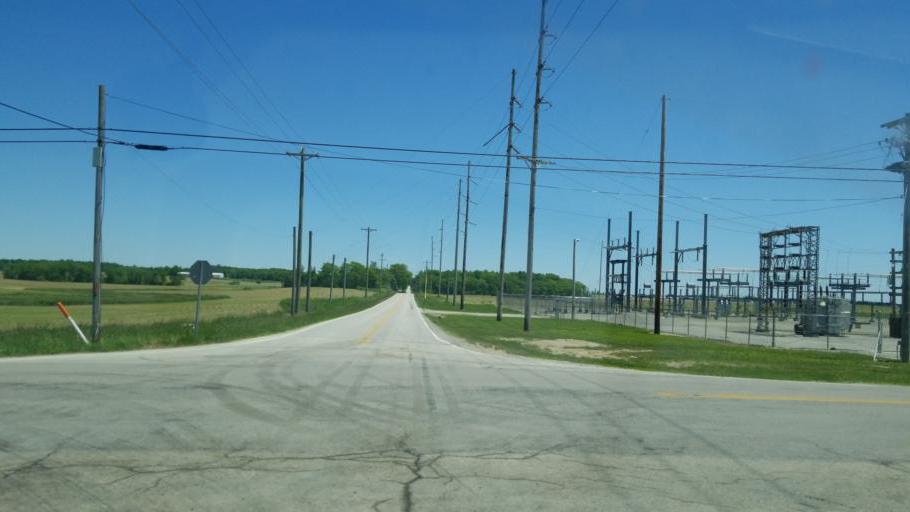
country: US
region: Ohio
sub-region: Darke County
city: Ansonia
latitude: 40.2647
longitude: -84.6366
